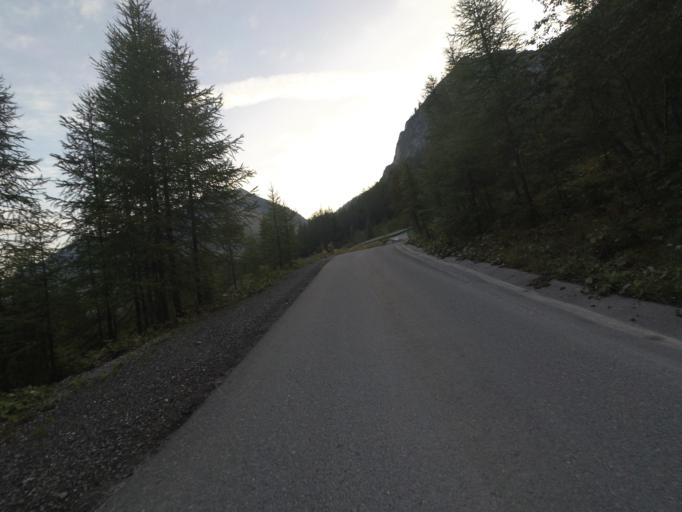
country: AT
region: Salzburg
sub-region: Politischer Bezirk Sankt Johann im Pongau
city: Untertauern
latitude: 47.2376
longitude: 13.4238
